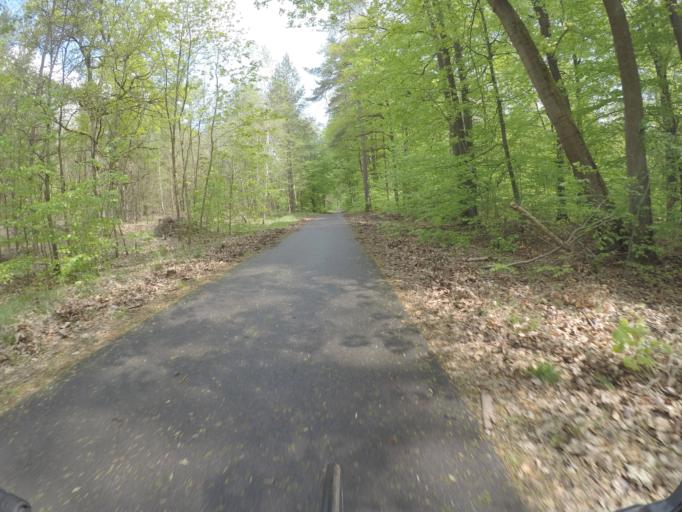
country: DE
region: Brandenburg
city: Joachimsthal
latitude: 52.9618
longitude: 13.7387
